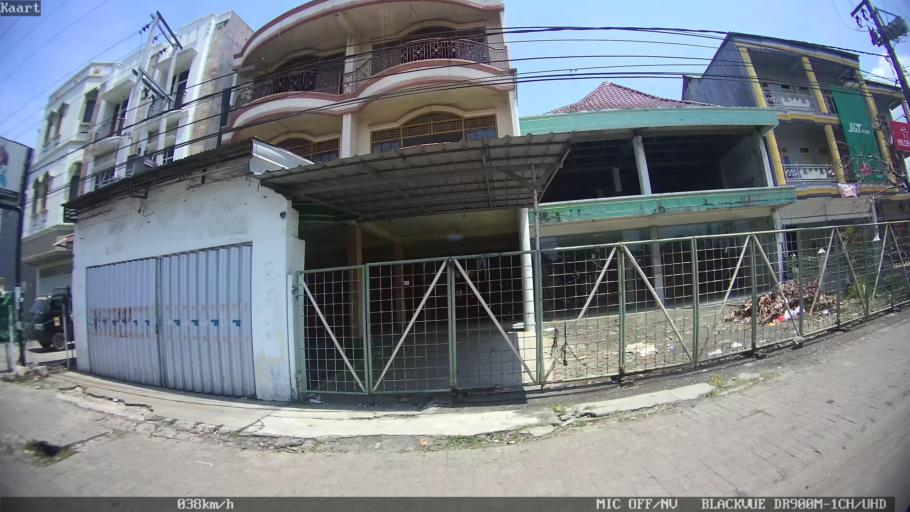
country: ID
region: Lampung
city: Bandarlampung
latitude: -5.4081
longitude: 105.2725
